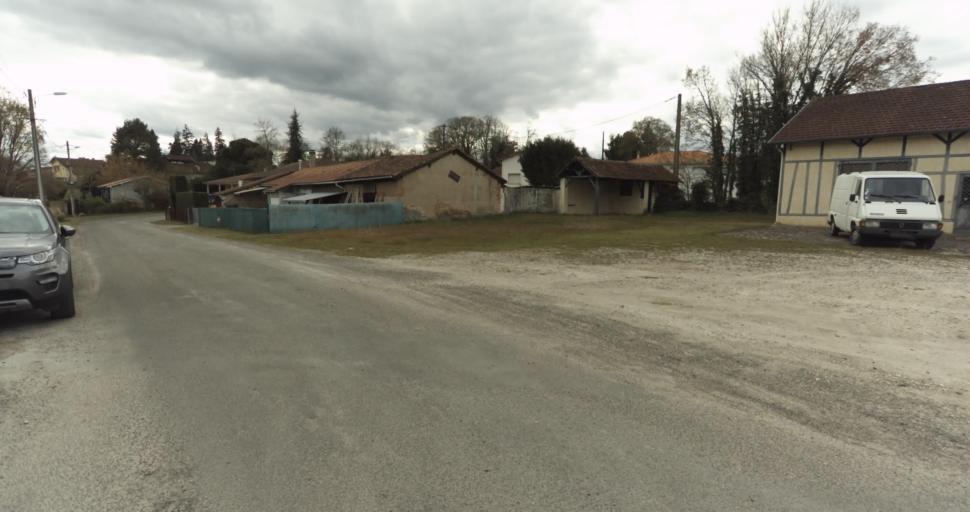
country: FR
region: Aquitaine
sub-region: Departement des Landes
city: Roquefort
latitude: 44.0398
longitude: -0.3217
